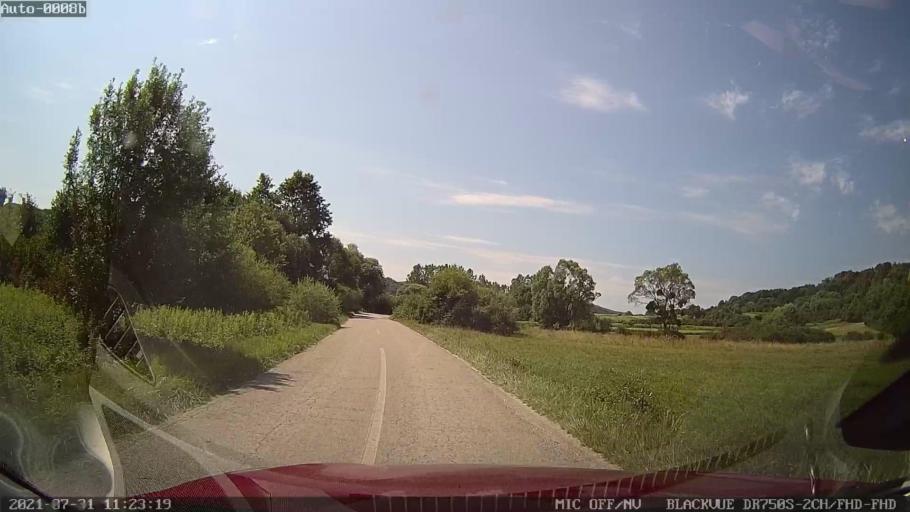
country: HR
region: Varazdinska
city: Jalzabet
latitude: 46.2172
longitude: 16.4627
